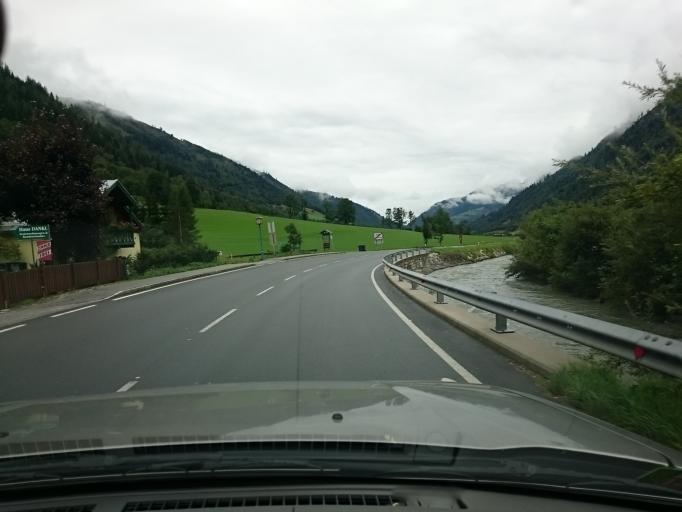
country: AT
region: Salzburg
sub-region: Politischer Bezirk Zell am See
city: Bruck an der Grossglocknerstrasse
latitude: 47.2327
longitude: 12.8252
